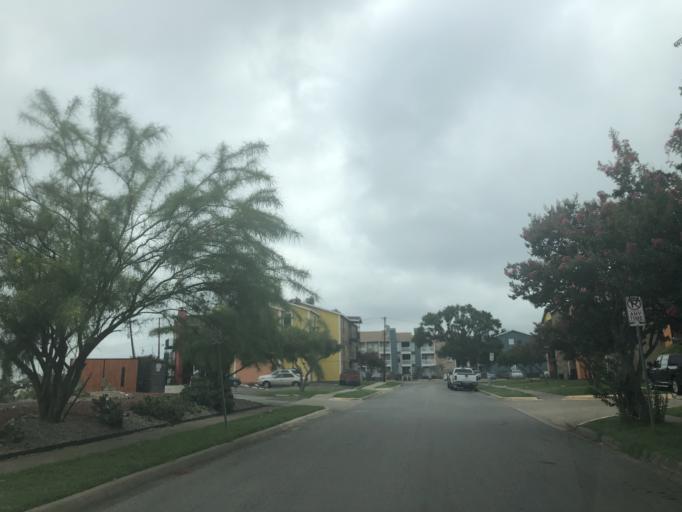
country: US
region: Texas
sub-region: Dallas County
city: University Park
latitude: 32.8610
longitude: -96.8655
